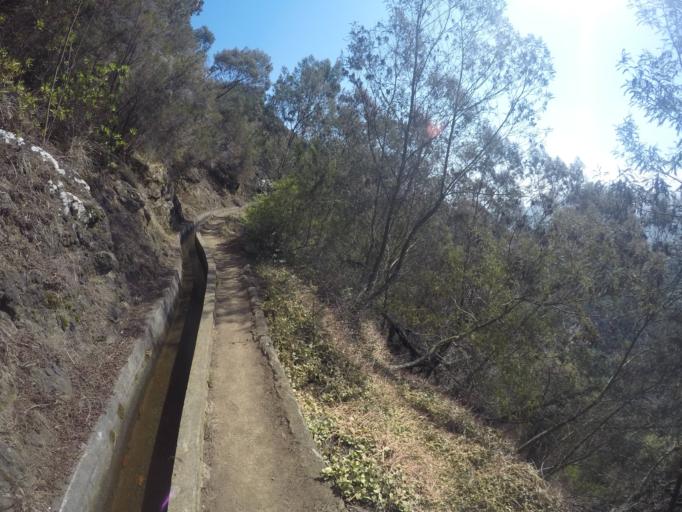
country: PT
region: Madeira
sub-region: Santana
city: Santana
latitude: 32.7543
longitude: -16.8403
